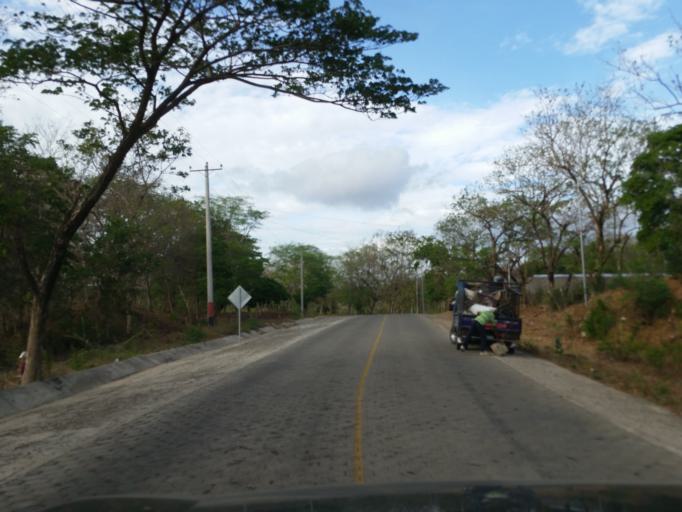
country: NI
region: Rivas
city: Tola
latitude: 11.4015
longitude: -85.9572
